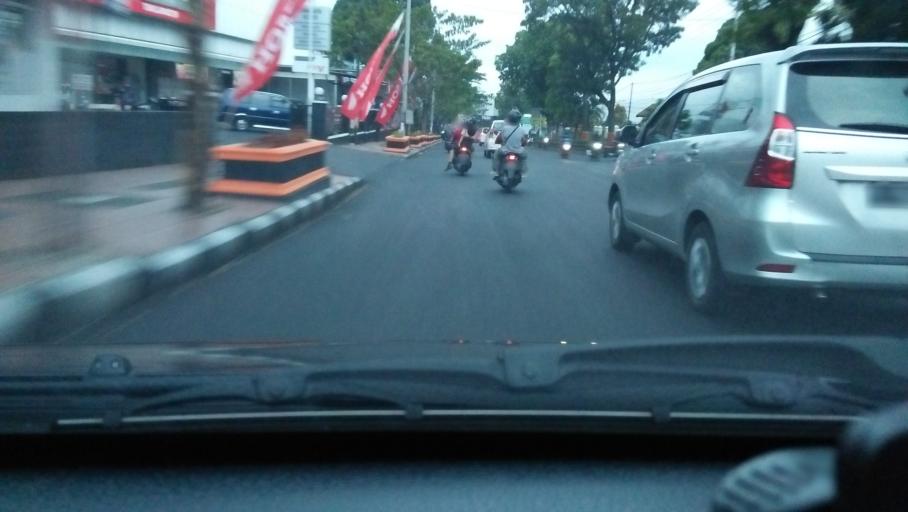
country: ID
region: Central Java
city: Mertoyudan
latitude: -7.4999
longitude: 110.2235
